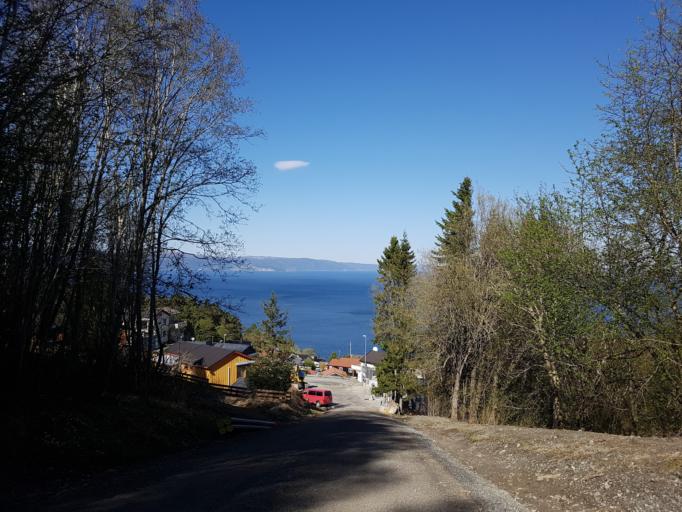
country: NO
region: Sor-Trondelag
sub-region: Trondheim
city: Trondheim
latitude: 63.4484
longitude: 10.3020
